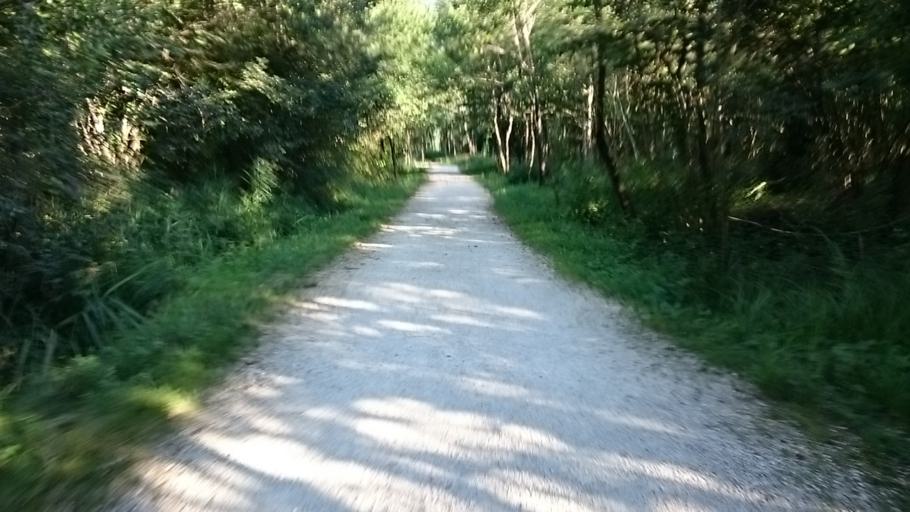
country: IT
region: Veneto
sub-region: Provincia di Belluno
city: Farra d'Alpago
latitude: 46.1217
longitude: 12.3465
